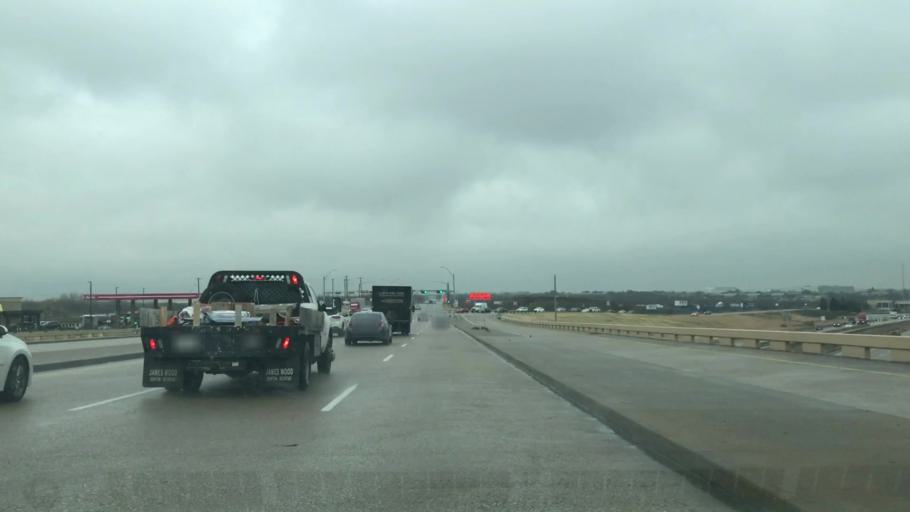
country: US
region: Texas
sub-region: Dallas County
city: Irving
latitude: 32.8772
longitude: -96.9914
